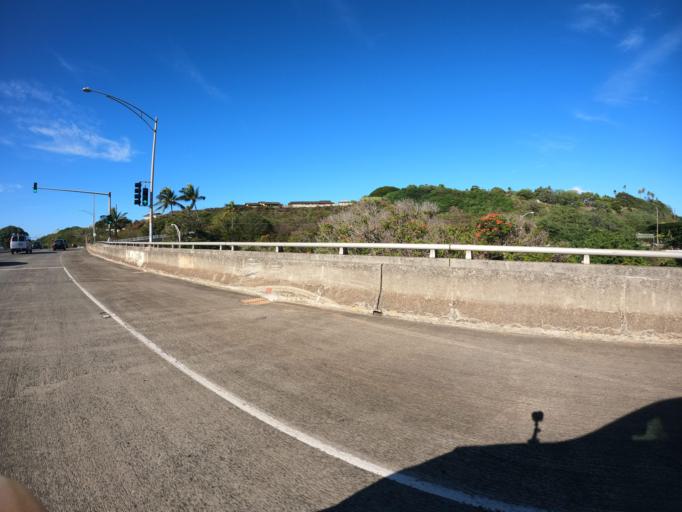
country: US
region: Hawaii
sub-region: Honolulu County
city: Halawa Heights
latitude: 21.3500
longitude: -157.8952
